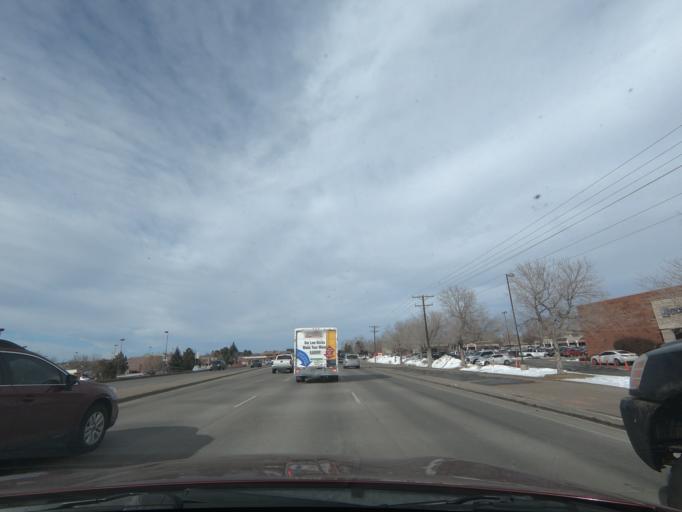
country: US
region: Colorado
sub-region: Douglas County
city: Parker
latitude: 39.5160
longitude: -104.7646
